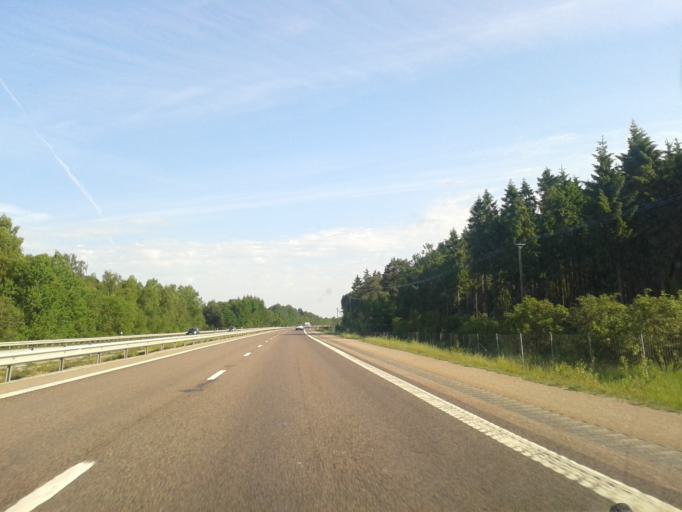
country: SE
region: Vaestra Goetaland
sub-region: Kungalvs Kommun
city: Kode
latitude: 57.9651
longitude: 11.8427
